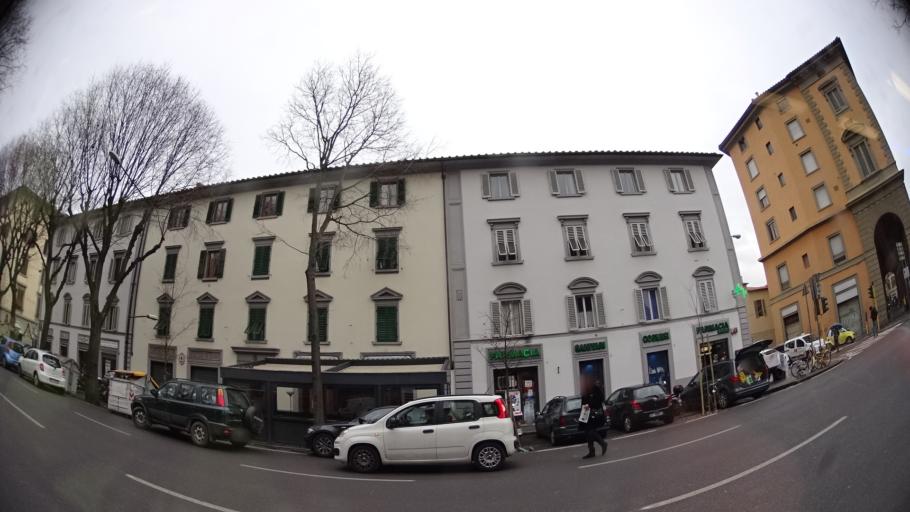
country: IT
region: Tuscany
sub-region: Province of Florence
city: Florence
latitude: 43.7855
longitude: 11.2657
